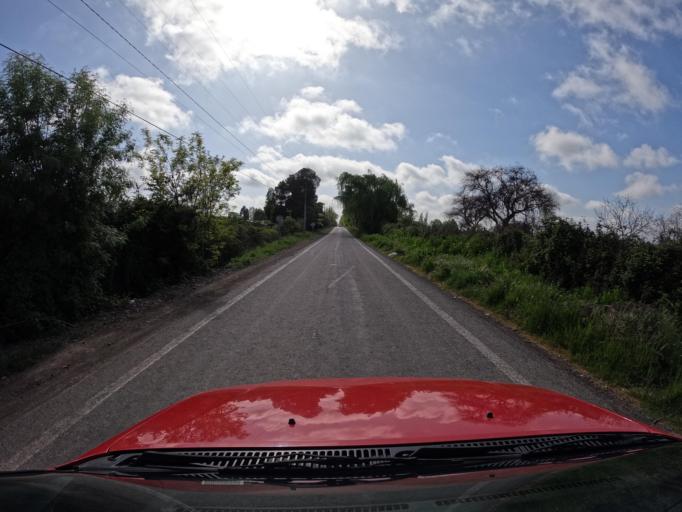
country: CL
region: Maule
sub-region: Provincia de Curico
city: Rauco
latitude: -34.8882
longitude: -71.2708
